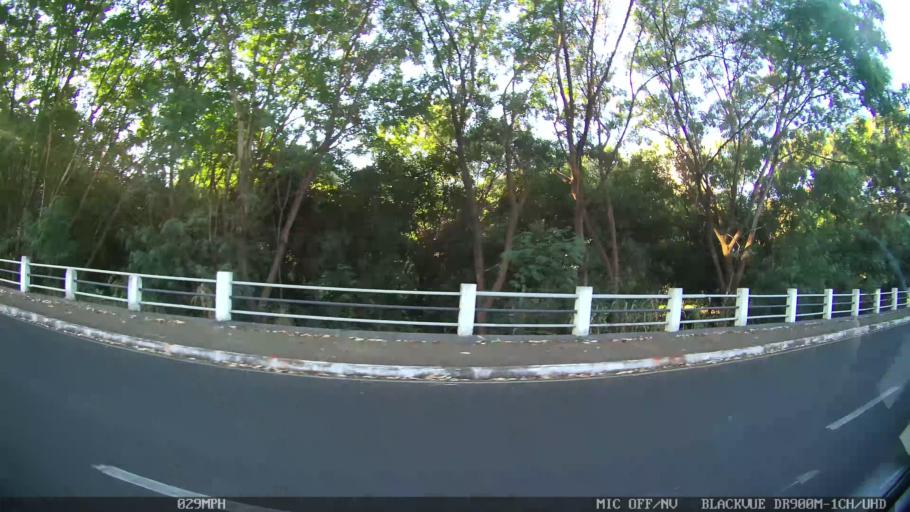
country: BR
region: Sao Paulo
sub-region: Sao Jose Do Rio Preto
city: Sao Jose do Rio Preto
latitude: -20.7868
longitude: -49.3699
